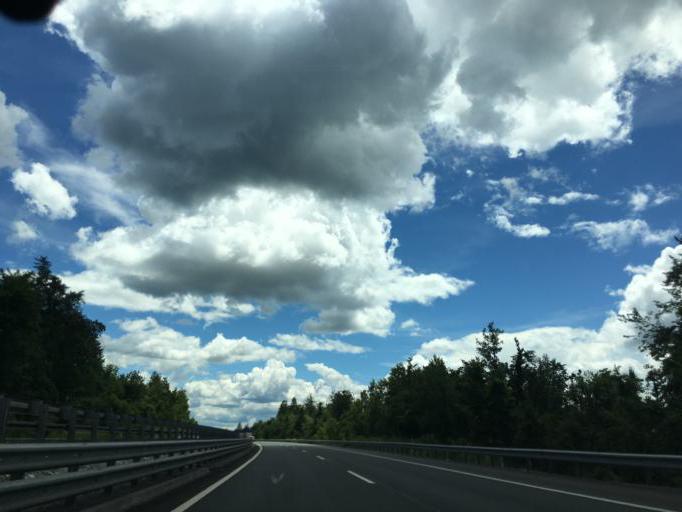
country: SI
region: Cerknica
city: Rakek
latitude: 45.8631
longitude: 14.2724
